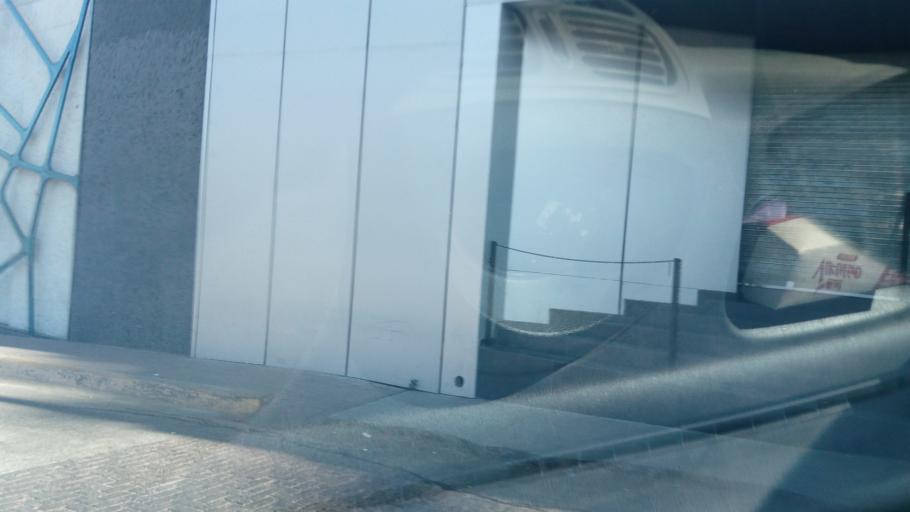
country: MX
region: Durango
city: Victoria de Durango
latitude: 24.0163
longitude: -104.6909
